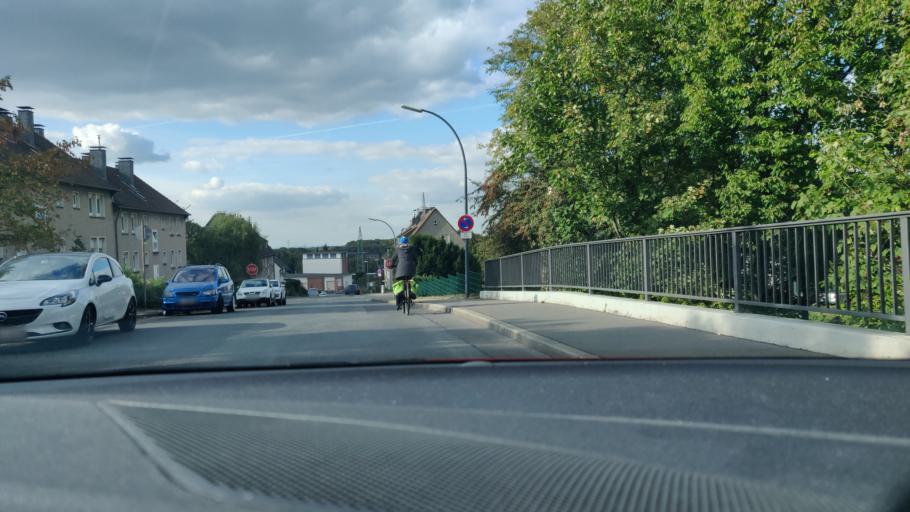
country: DE
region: North Rhine-Westphalia
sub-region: Regierungsbezirk Dusseldorf
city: Velbert
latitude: 51.3470
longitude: 7.0423
